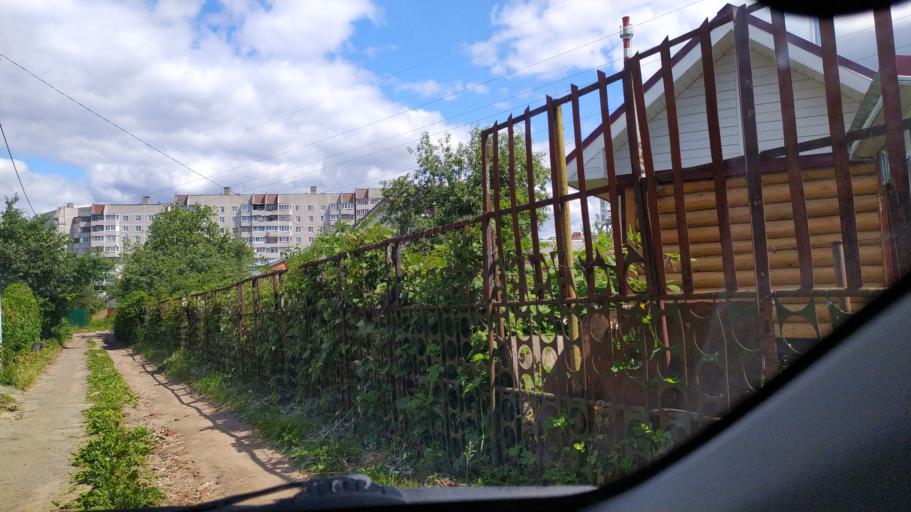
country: RU
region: Chuvashia
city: Novyye Lapsary
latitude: 56.1158
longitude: 47.1748
